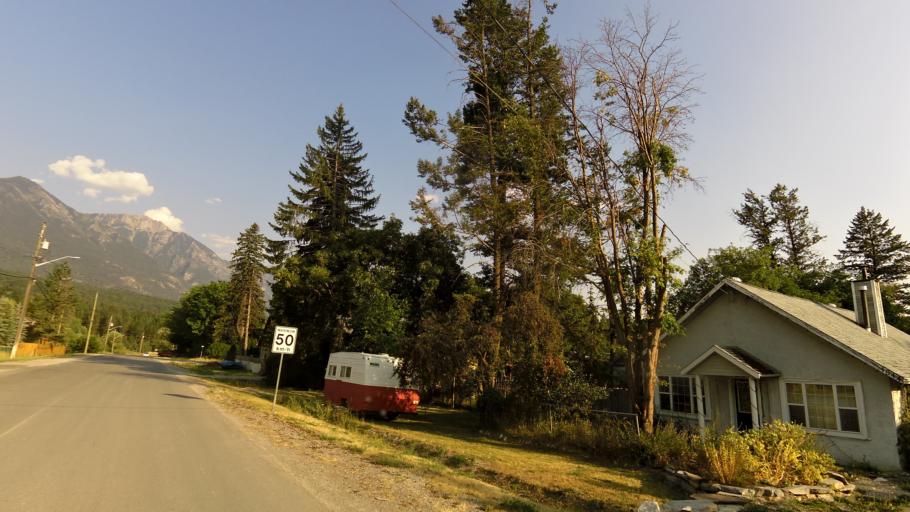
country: CA
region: British Columbia
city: Invermere
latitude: 50.6975
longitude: -116.1328
